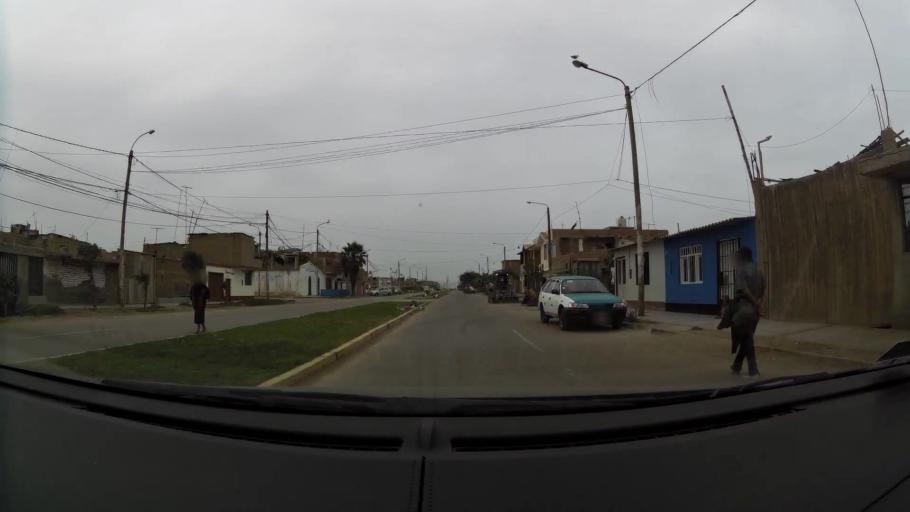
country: PE
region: La Libertad
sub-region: Provincia de Trujillo
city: Buenos Aires
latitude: -8.1469
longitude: -79.0489
